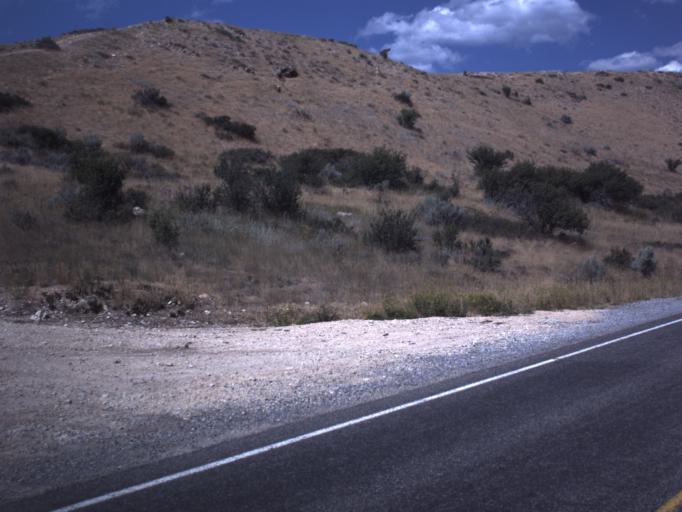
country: US
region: Utah
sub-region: Rich County
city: Randolph
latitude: 41.8772
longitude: -111.3653
